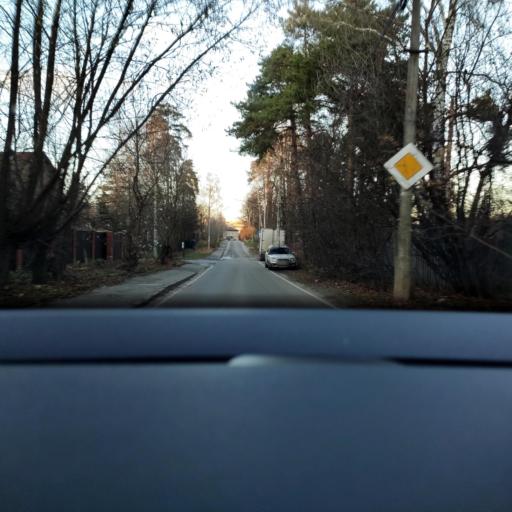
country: RU
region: Moskovskaya
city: Vidnoye
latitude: 55.5454
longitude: 37.6843
